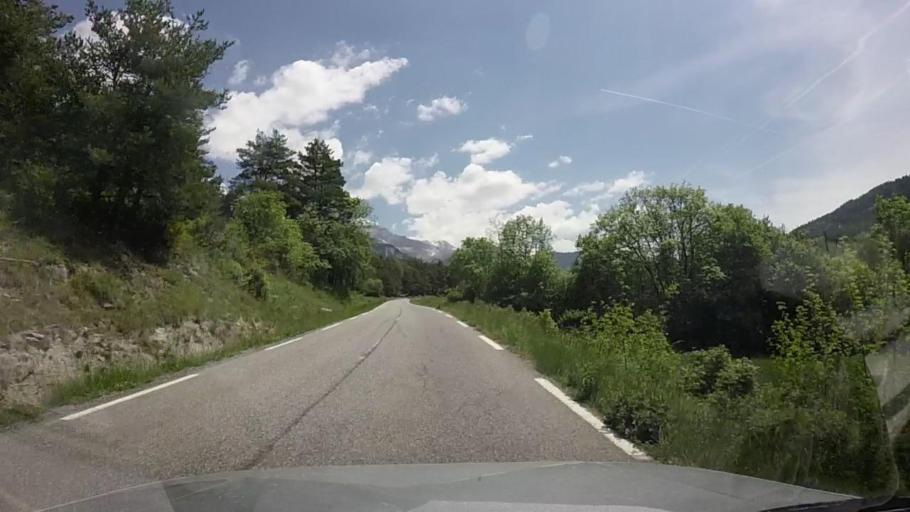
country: FR
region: Provence-Alpes-Cote d'Azur
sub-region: Departement des Alpes-de-Haute-Provence
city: Seyne-les-Alpes
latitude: 44.3377
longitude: 6.3835
